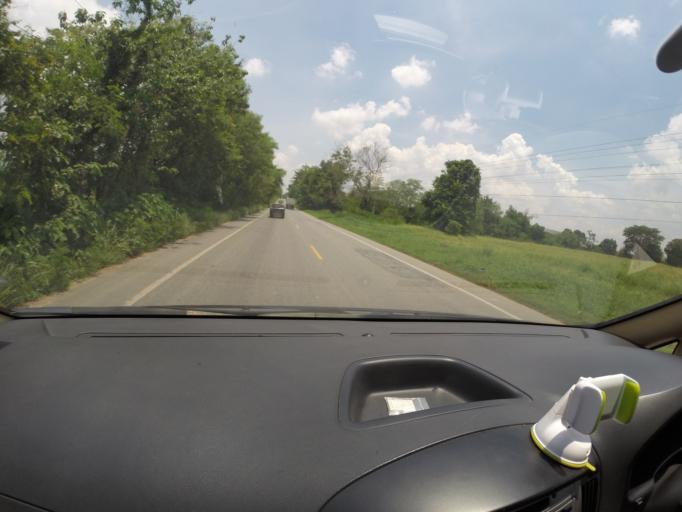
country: TH
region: Nakhon Ratchasima
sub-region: Amphoe Thepharak
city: Thepharak
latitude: 15.1258
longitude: 101.5422
